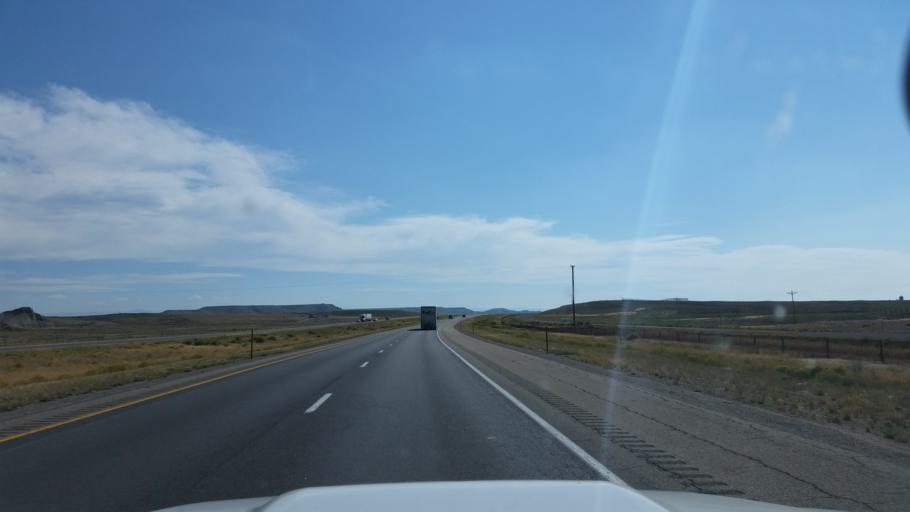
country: US
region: Wyoming
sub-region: Uinta County
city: Lyman
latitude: 41.4730
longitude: -110.0368
